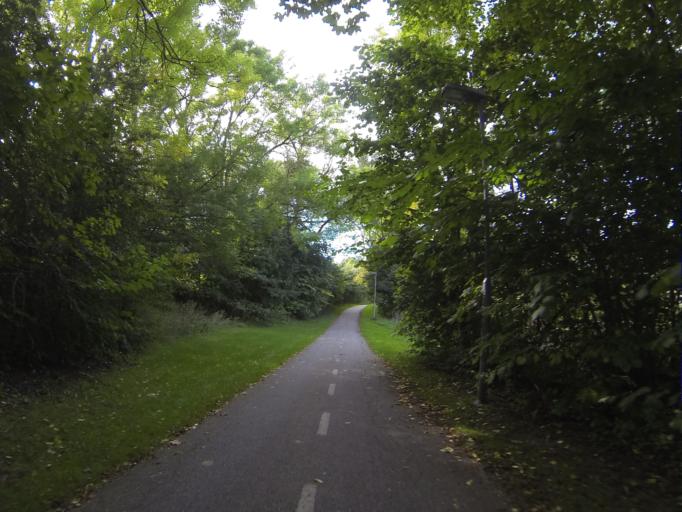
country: SE
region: Skane
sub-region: Lunds Kommun
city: Genarp
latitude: 55.7130
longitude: 13.3351
